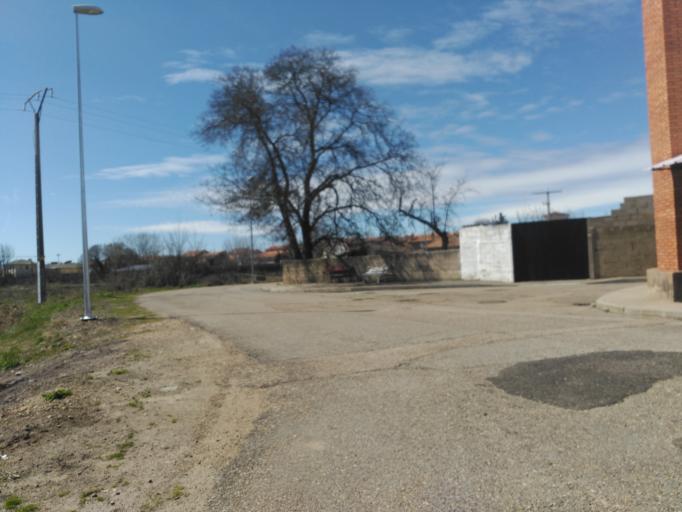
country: ES
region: Castille and Leon
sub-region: Provincia de Leon
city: Hospital de Orbigo
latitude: 42.4408
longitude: -5.8803
